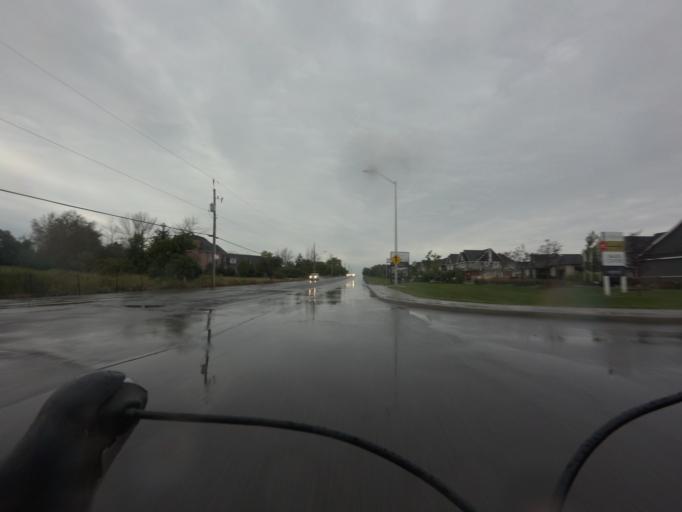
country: CA
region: Ontario
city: Bells Corners
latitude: 45.2499
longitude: -75.7167
